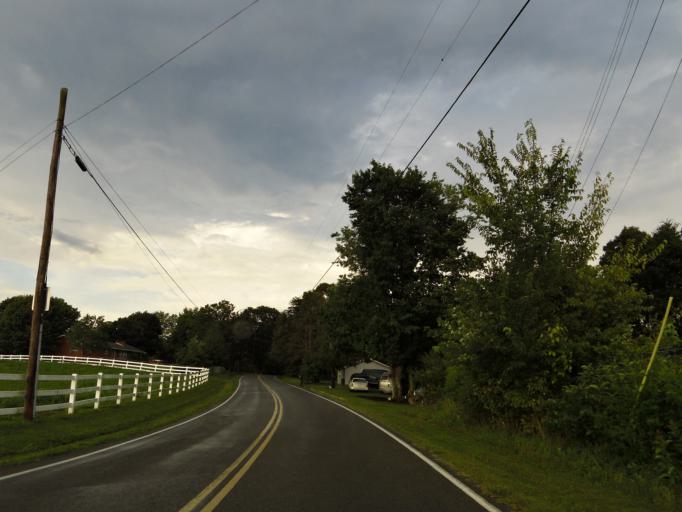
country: US
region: Tennessee
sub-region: Sevier County
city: Seymour
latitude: 35.8443
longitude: -83.7637
